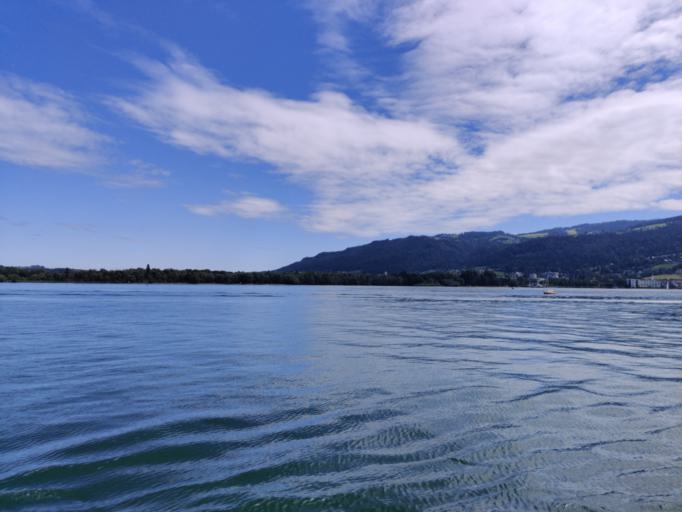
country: AT
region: Vorarlberg
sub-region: Politischer Bezirk Bregenz
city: Lochau
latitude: 47.5248
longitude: 9.7266
